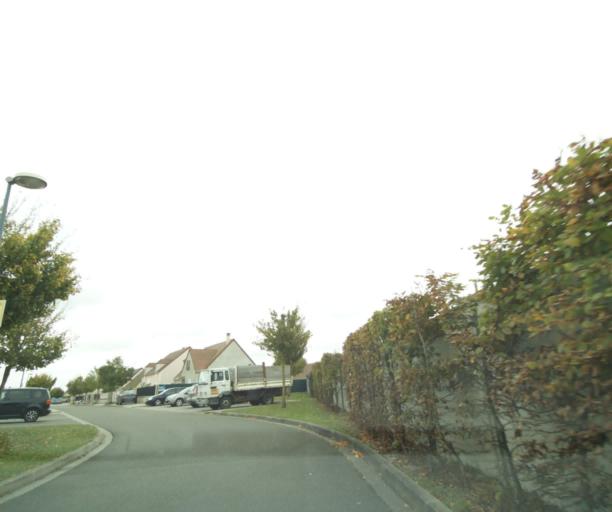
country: FR
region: Centre
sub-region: Departement d'Eure-et-Loir
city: Dreux
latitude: 48.7375
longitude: 1.3507
